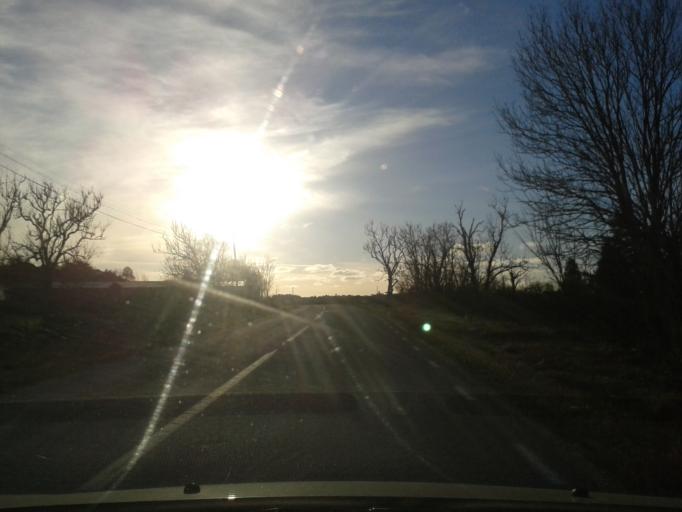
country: SE
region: Gotland
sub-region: Gotland
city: Hemse
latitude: 57.4168
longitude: 18.6322
